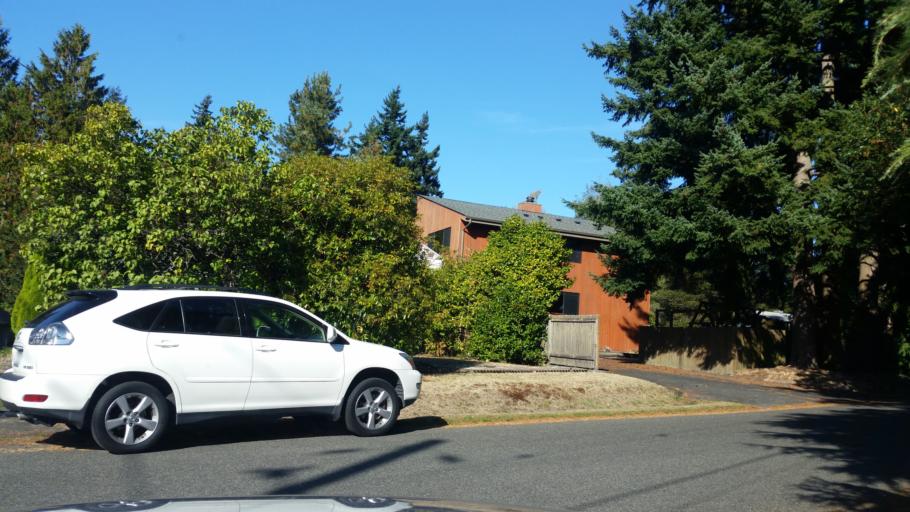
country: US
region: Washington
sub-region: King County
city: Shoreline
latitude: 47.7104
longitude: -122.3595
